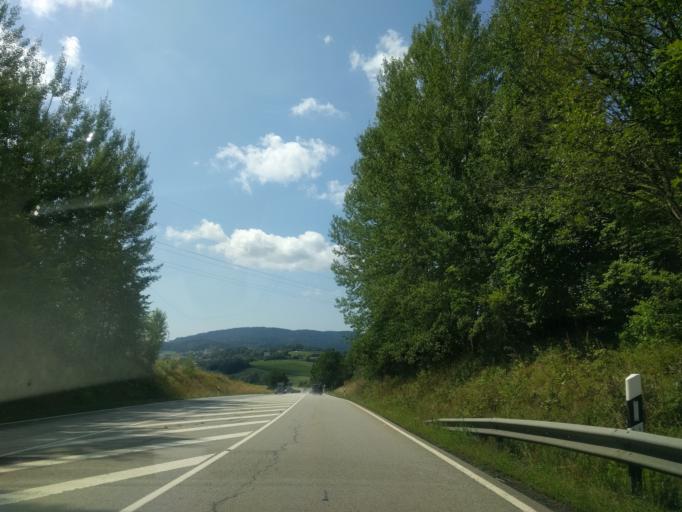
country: DE
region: Bavaria
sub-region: Lower Bavaria
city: Grafenau
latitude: 48.8351
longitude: 13.3644
